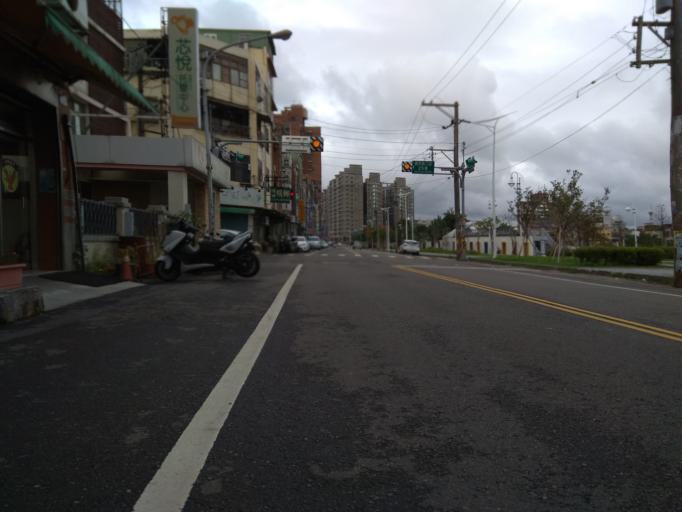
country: TW
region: Taiwan
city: Taoyuan City
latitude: 24.9589
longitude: 121.2181
